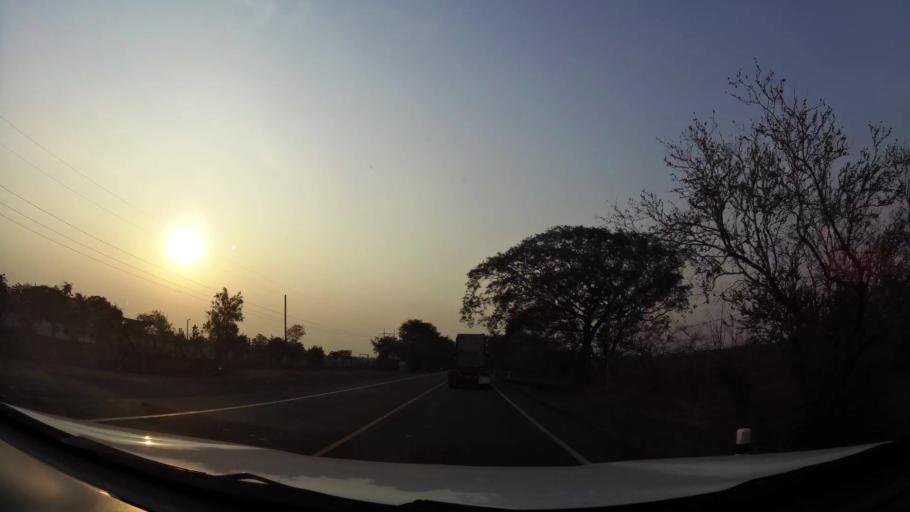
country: NI
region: Leon
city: Nagarote
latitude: 12.2795
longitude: -86.5786
